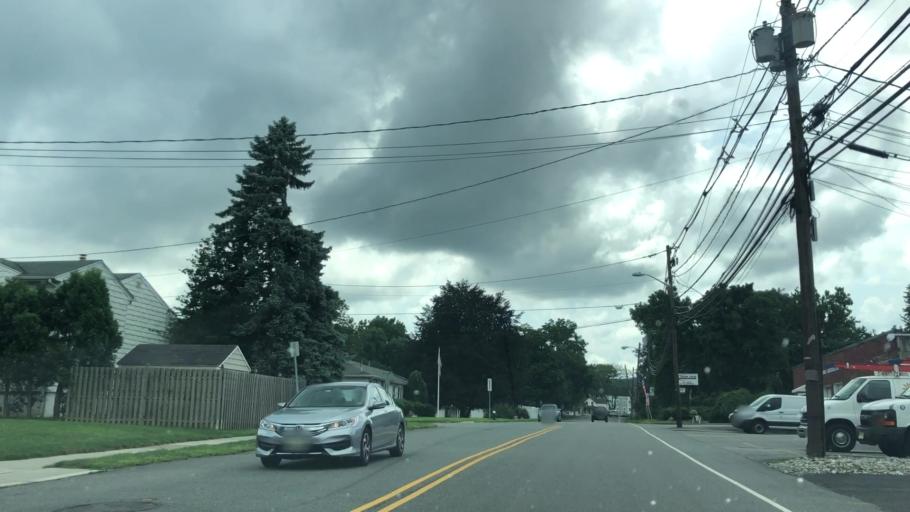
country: US
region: New Jersey
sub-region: Passaic County
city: Singac
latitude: 40.8846
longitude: -74.2233
